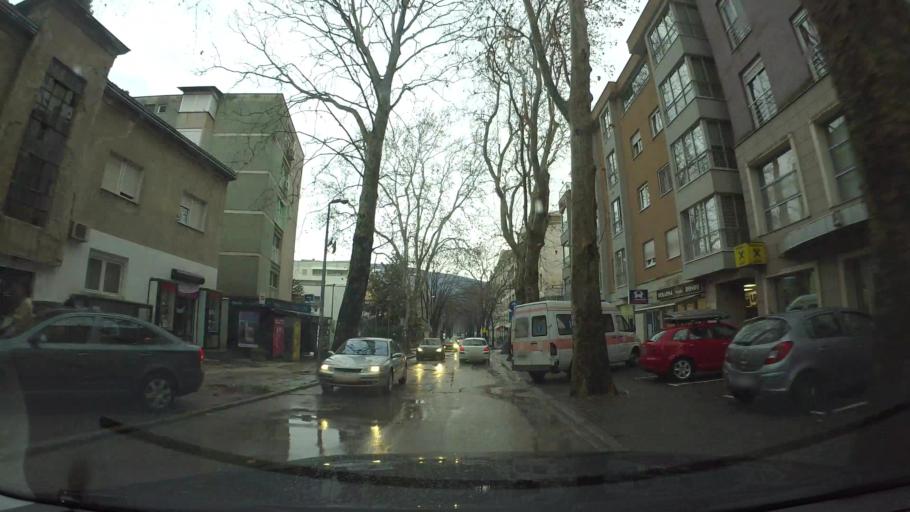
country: BA
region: Federation of Bosnia and Herzegovina
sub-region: Hercegovacko-Bosanski Kanton
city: Mostar
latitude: 43.3424
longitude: 17.7998
